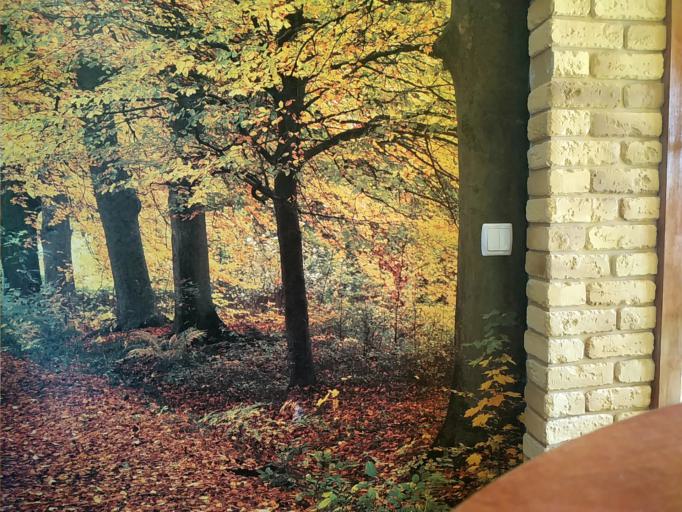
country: RU
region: Jaroslavl
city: Kukoboy
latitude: 58.9231
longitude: 39.6738
